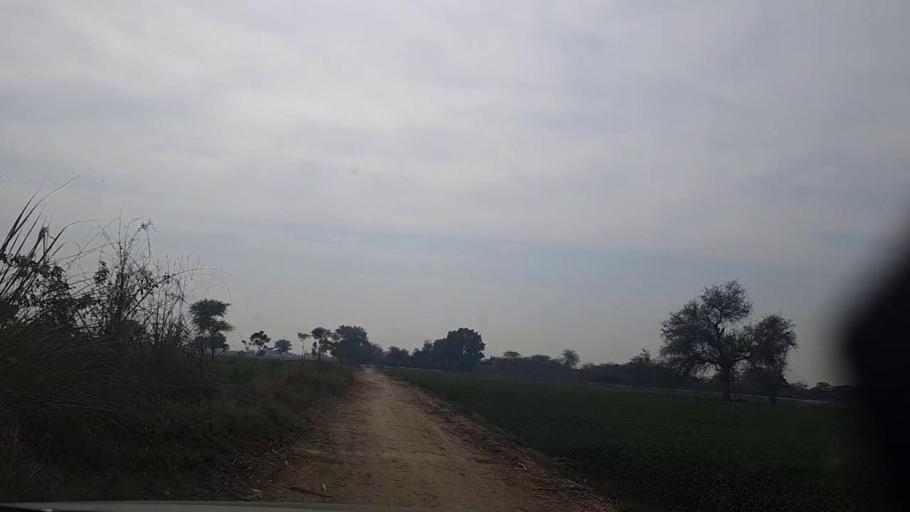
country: PK
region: Sindh
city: Sakrand
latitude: 26.2277
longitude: 68.2970
